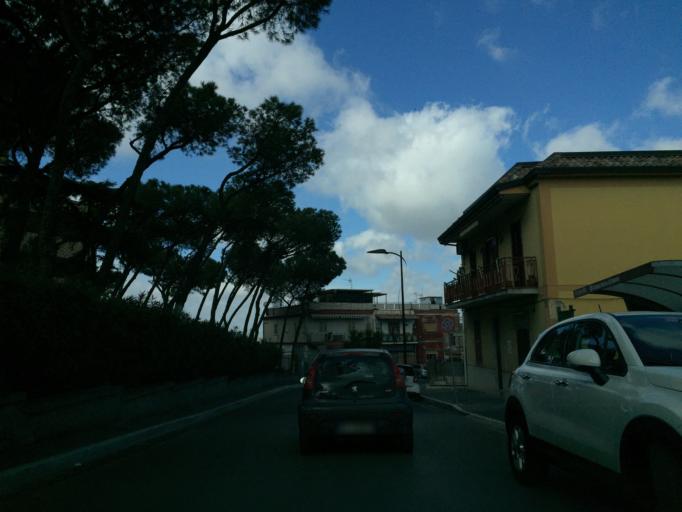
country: IT
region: Campania
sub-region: Provincia di Napoli
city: Massa di Somma
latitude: 40.8467
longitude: 14.3731
